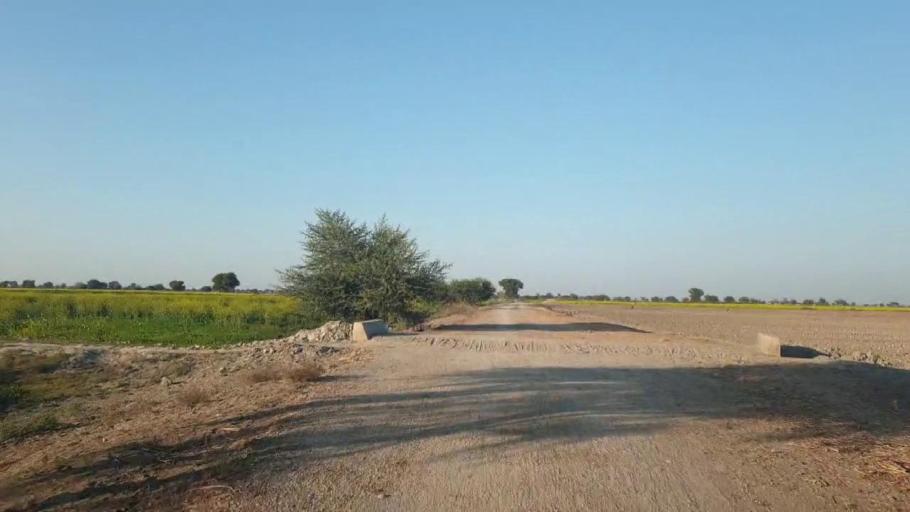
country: PK
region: Sindh
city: Shahpur Chakar
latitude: 26.0699
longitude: 68.6556
